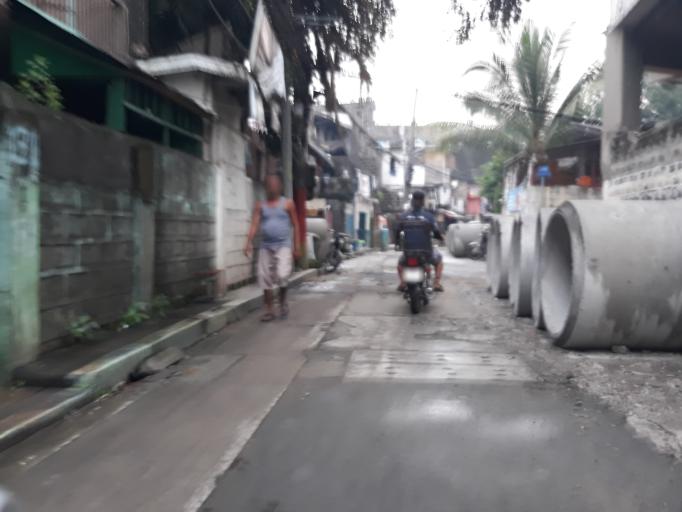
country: PH
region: Metro Manila
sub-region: San Juan
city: San Juan
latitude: 14.6113
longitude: 121.0228
